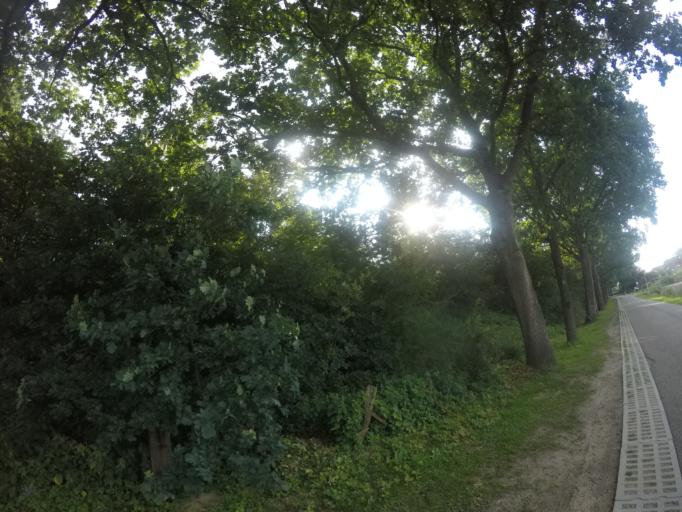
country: NL
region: Gelderland
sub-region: Gemeente Westervoort
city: Westervoort
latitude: 51.9603
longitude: 5.9753
